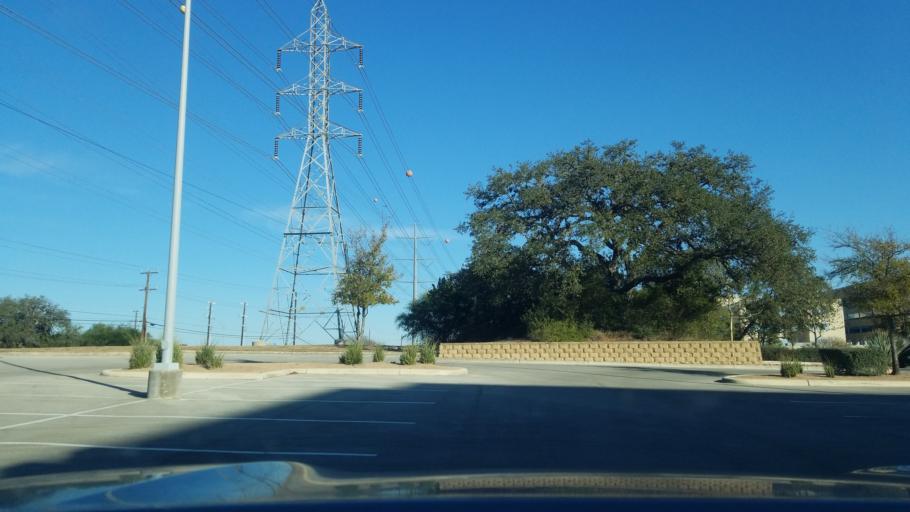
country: US
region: Texas
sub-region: Bexar County
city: Hollywood Park
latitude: 29.6167
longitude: -98.4778
